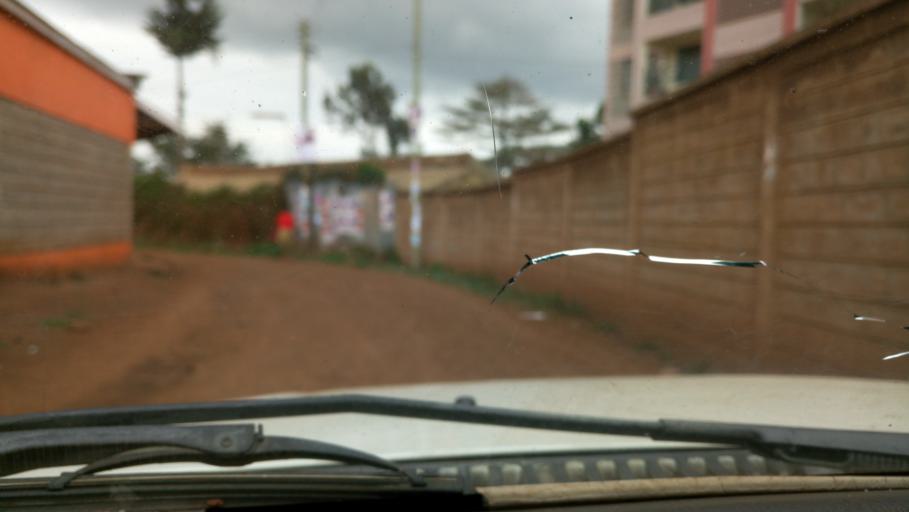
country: KE
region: Kiambu
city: Kikuyu
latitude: -1.2580
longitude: 36.7203
